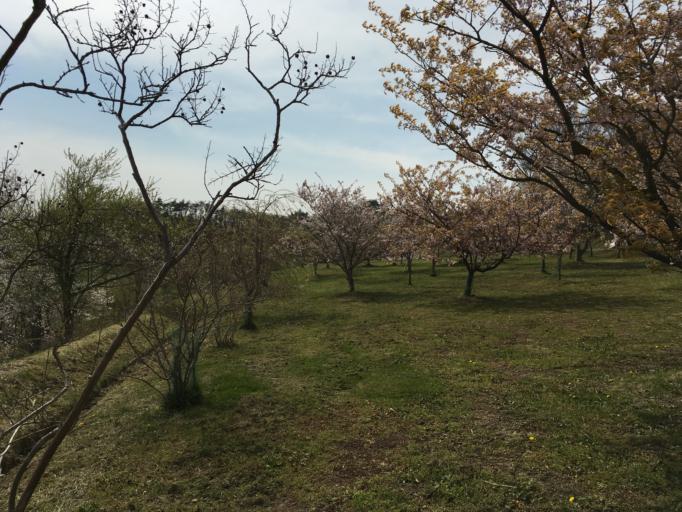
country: JP
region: Iwate
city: Ichinoseki
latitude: 38.8236
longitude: 141.2711
